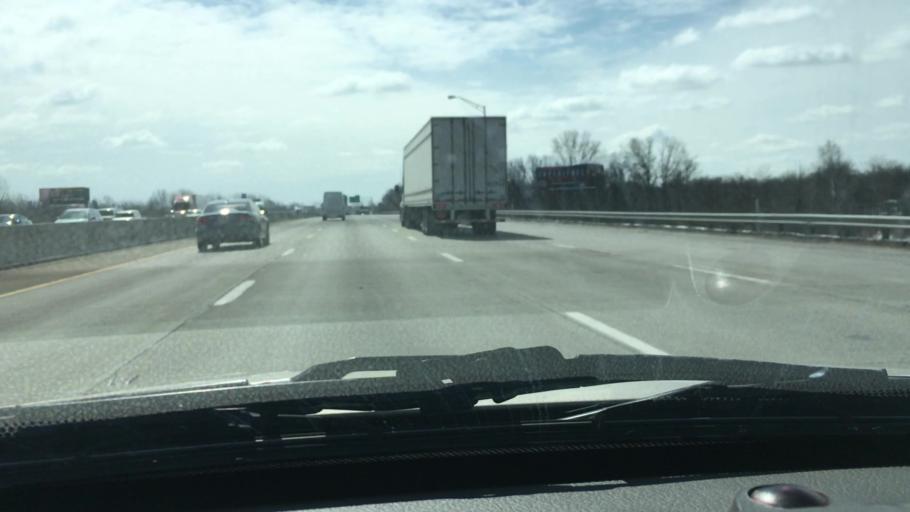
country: US
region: Indiana
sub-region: Marion County
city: Warren Park
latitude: 39.7719
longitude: -86.0303
